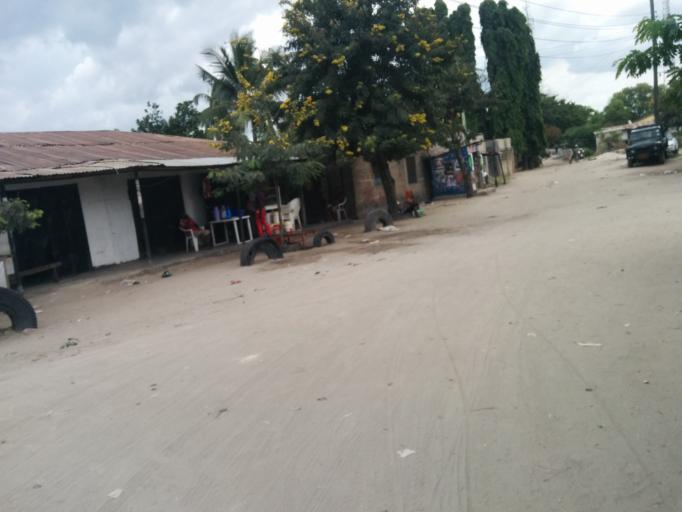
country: TZ
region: Dar es Salaam
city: Dar es Salaam
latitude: -6.8616
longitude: 39.2570
